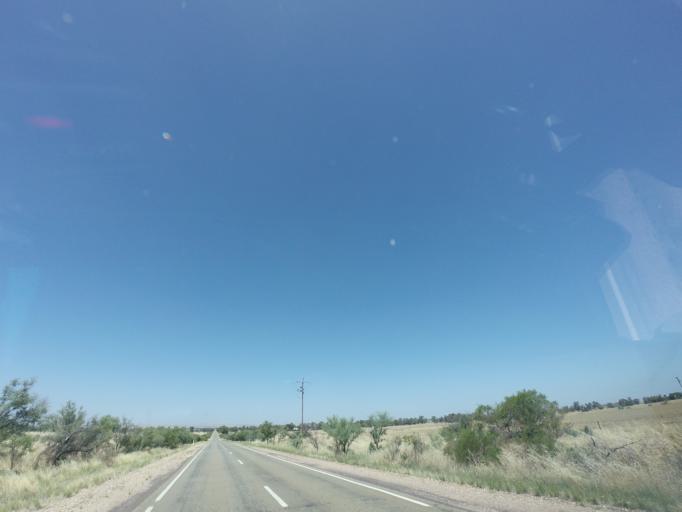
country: AU
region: South Australia
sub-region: Flinders Ranges
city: Quorn
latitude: -32.6662
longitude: 138.1362
